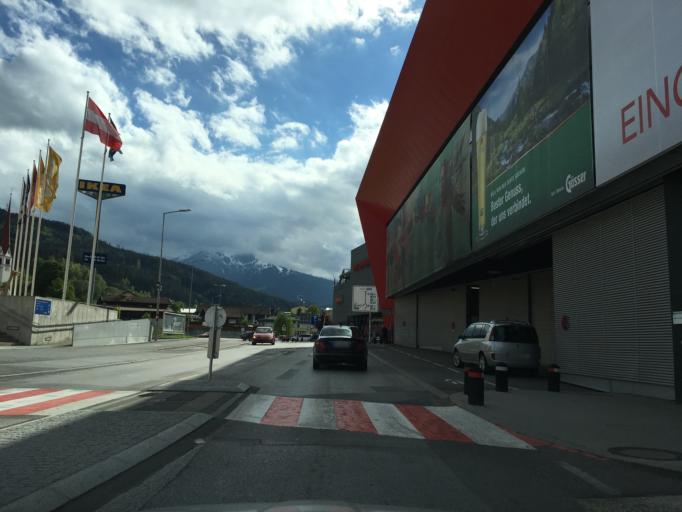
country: AT
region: Tyrol
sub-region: Politischer Bezirk Innsbruck Land
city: Ampass
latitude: 47.2621
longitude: 11.4313
